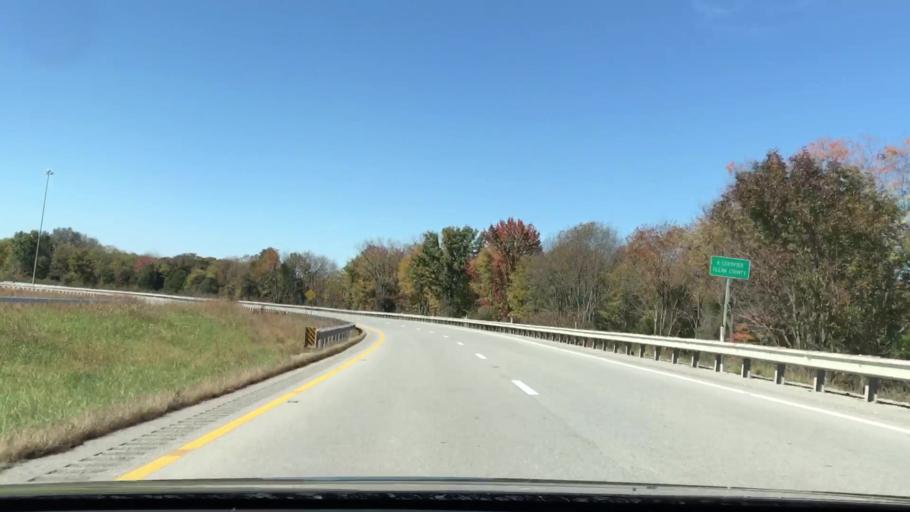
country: US
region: Kentucky
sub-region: Barren County
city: Cave City
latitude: 37.0591
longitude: -86.1138
